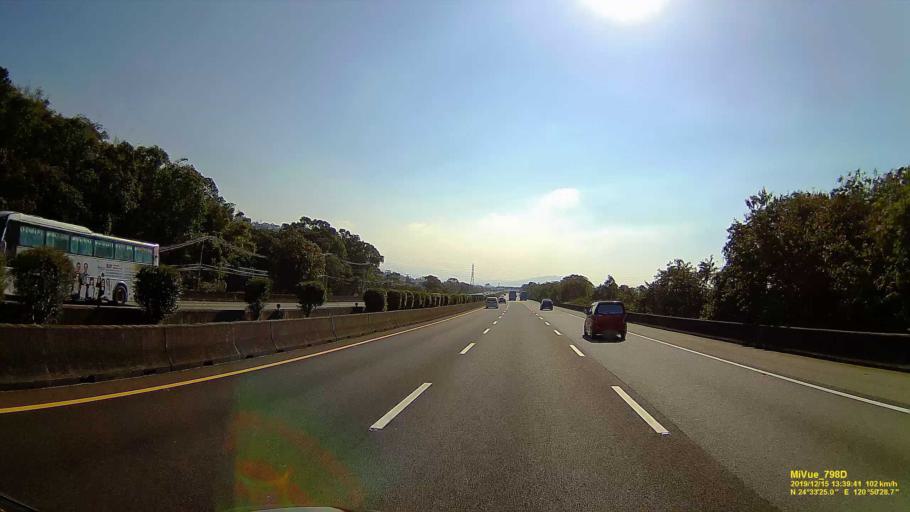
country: TW
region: Taiwan
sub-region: Miaoli
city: Miaoli
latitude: 24.5565
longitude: 120.8410
